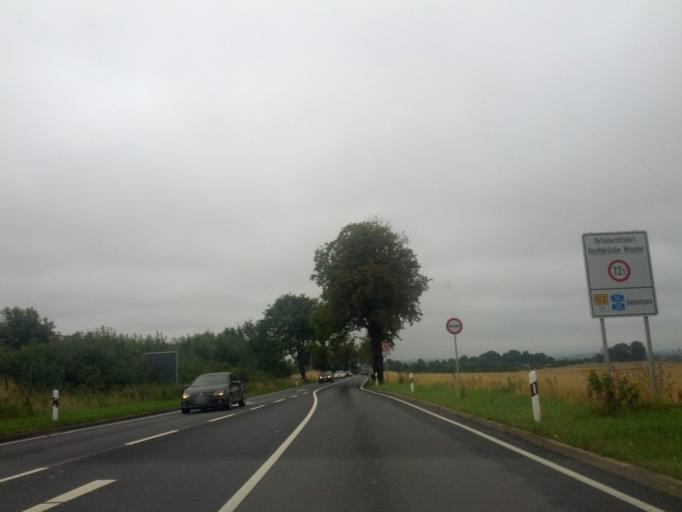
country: DE
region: Mecklenburg-Vorpommern
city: Hornstorf
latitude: 53.8954
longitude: 11.5400
